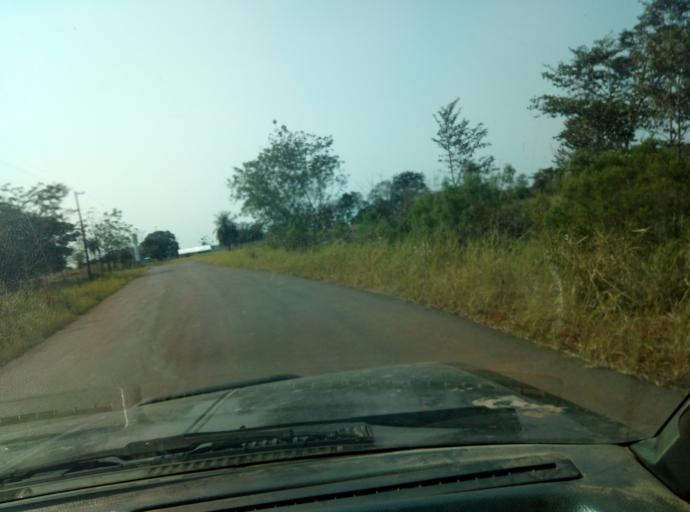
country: PY
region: Caaguazu
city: Carayao
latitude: -25.2354
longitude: -56.2884
